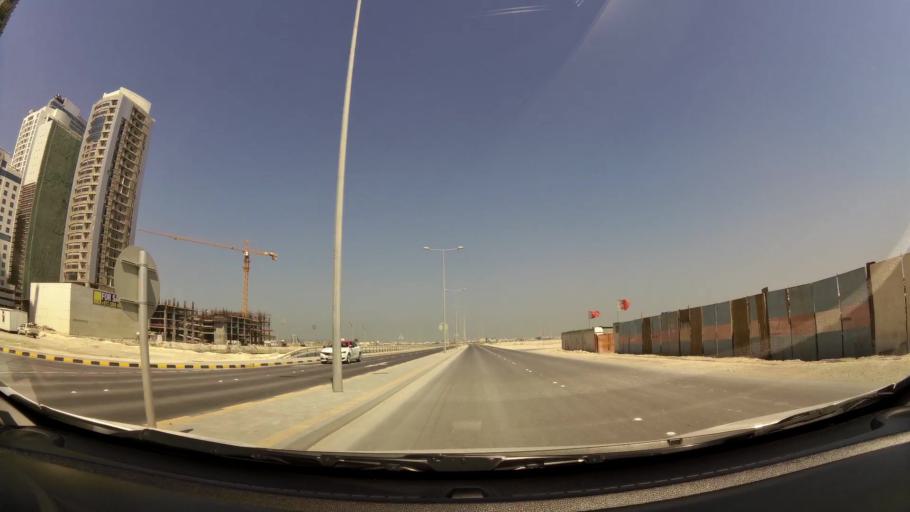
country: BH
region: Manama
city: Manama
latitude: 26.2216
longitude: 50.6126
